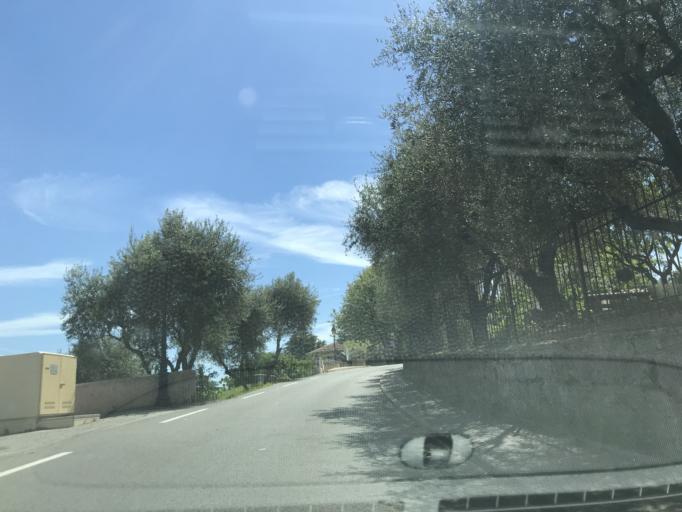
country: FR
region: Provence-Alpes-Cote d'Azur
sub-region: Departement du Var
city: Tanneron
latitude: 43.5912
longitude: 6.8748
